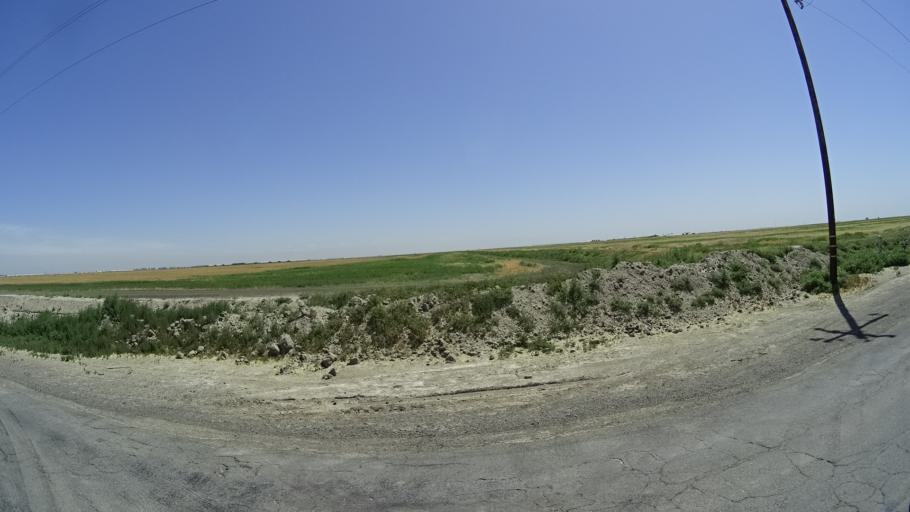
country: US
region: California
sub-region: Kings County
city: Stratford
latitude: 36.1747
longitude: -119.7175
